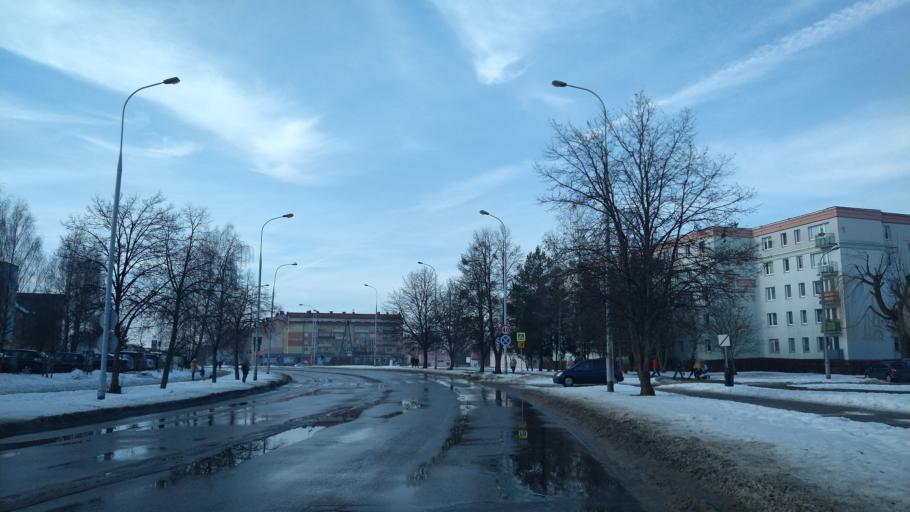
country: PL
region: Warmian-Masurian Voivodeship
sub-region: Powiat olsztynski
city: Olsztyn
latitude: 53.7423
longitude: 20.5125
